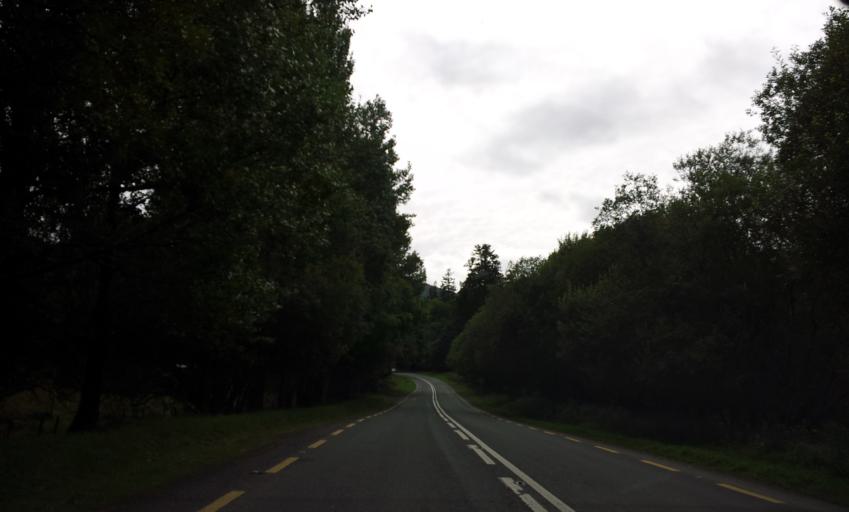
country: IE
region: Munster
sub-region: Ciarrai
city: Cill Airne
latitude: 52.0237
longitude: -9.4910
